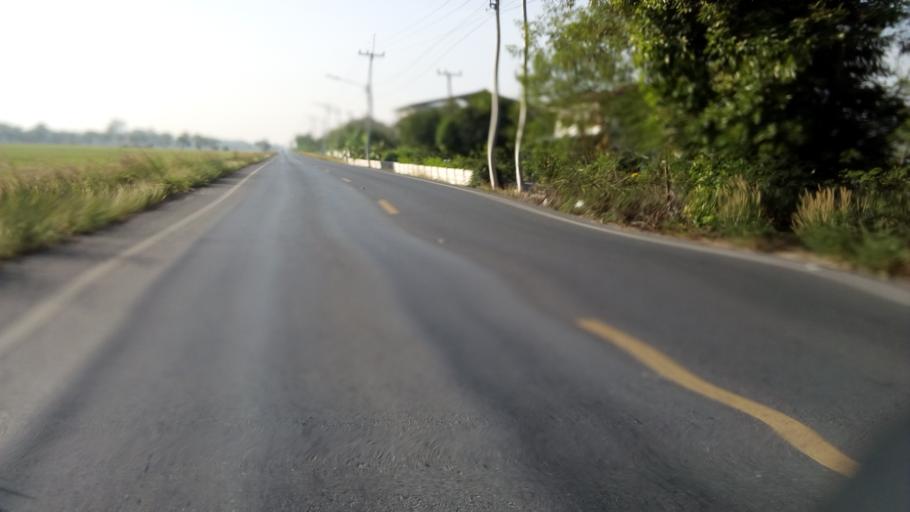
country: TH
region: Pathum Thani
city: Nong Suea
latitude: 14.0549
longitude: 100.8451
